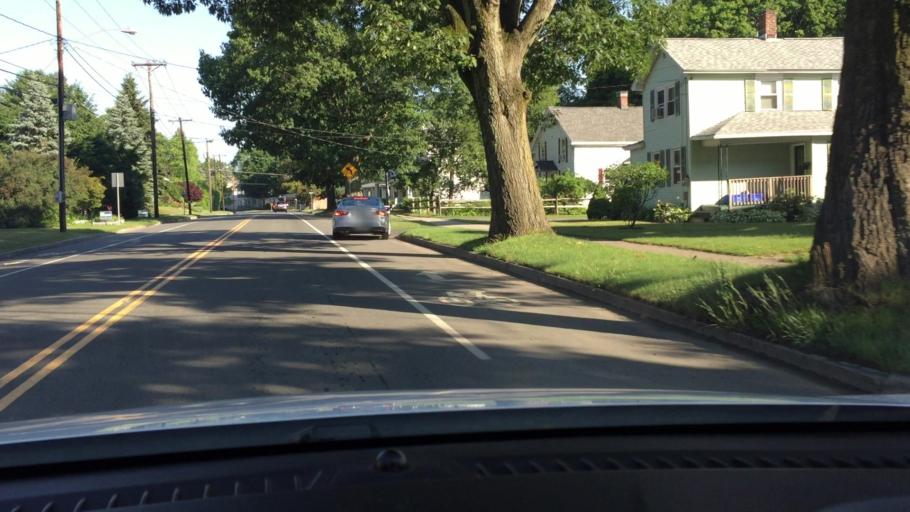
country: US
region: Massachusetts
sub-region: Berkshire County
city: Pittsfield
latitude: 42.4413
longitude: -73.2285
